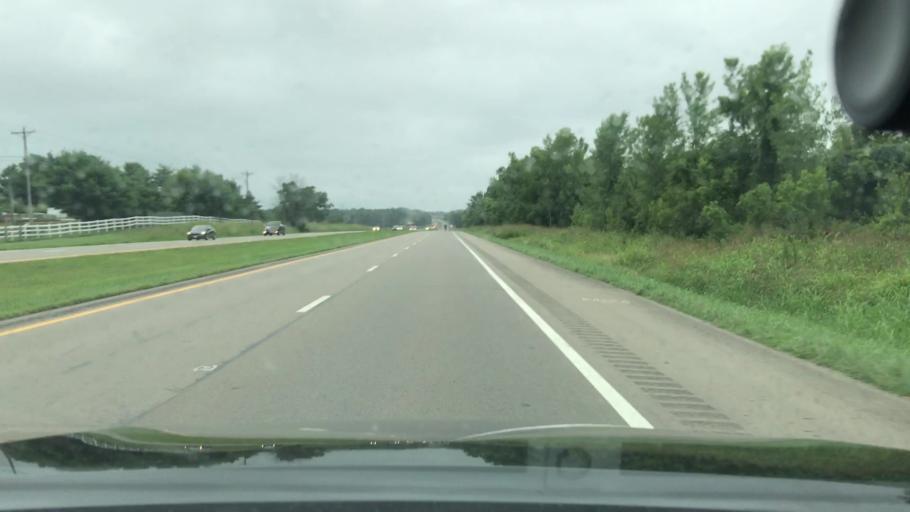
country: US
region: Ohio
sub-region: Ross County
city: Kingston
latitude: 39.4524
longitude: -82.9720
